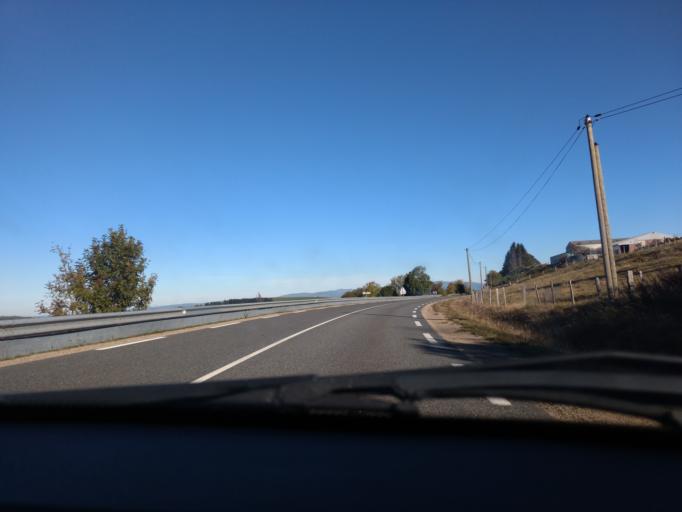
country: FR
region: Midi-Pyrenees
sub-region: Departement de l'Aveyron
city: Laguiole
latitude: 44.7460
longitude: 2.8712
